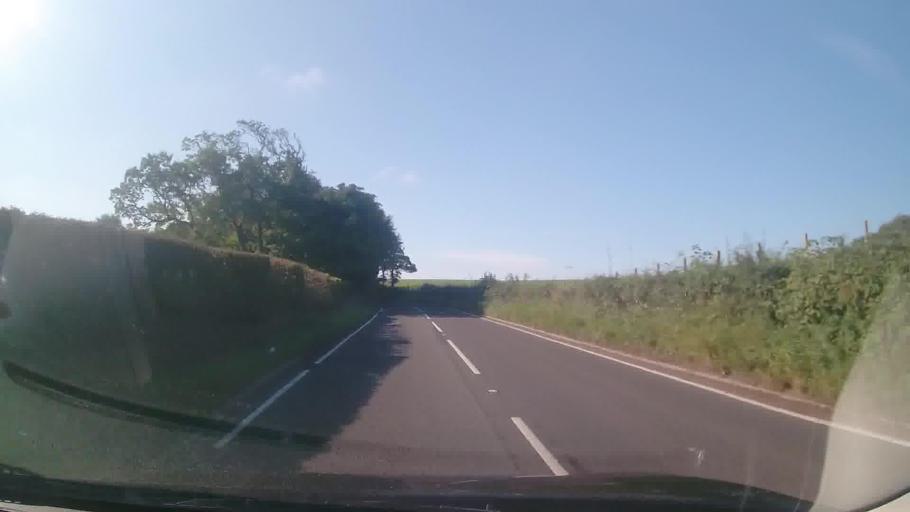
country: GB
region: England
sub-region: Cumbria
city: Seascale
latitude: 54.3792
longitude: -3.4142
